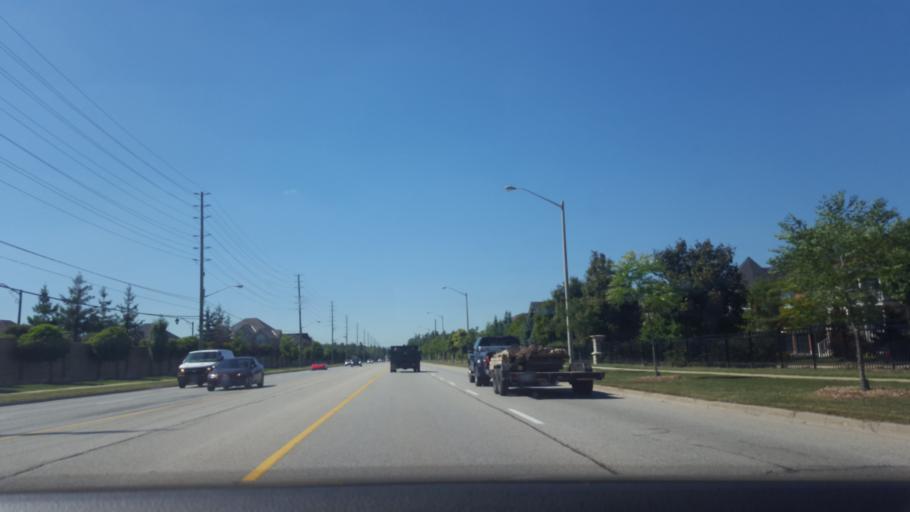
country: CA
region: Ontario
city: Vaughan
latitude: 43.8238
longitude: -79.5700
